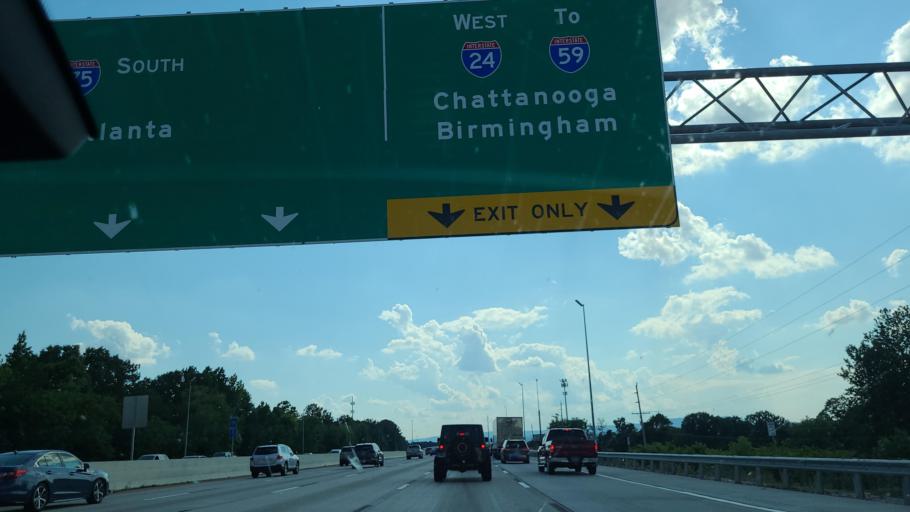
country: US
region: Tennessee
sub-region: Hamilton County
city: East Brainerd
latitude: 35.0078
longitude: -85.1997
